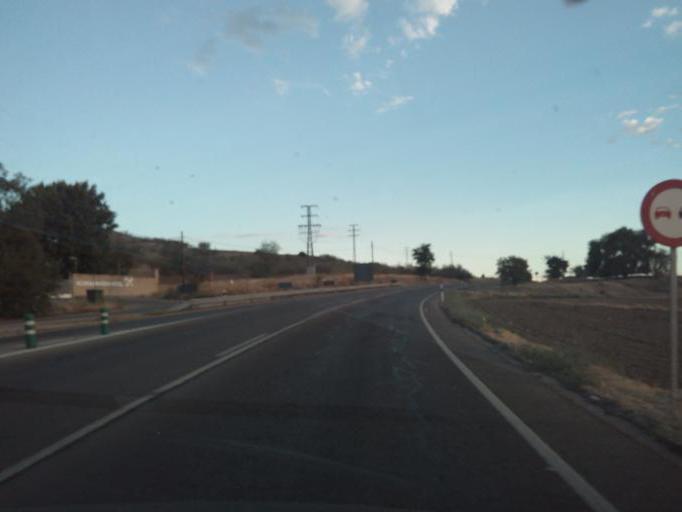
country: ES
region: Madrid
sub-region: Provincia de Madrid
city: Algete
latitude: 40.5928
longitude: -3.5073
